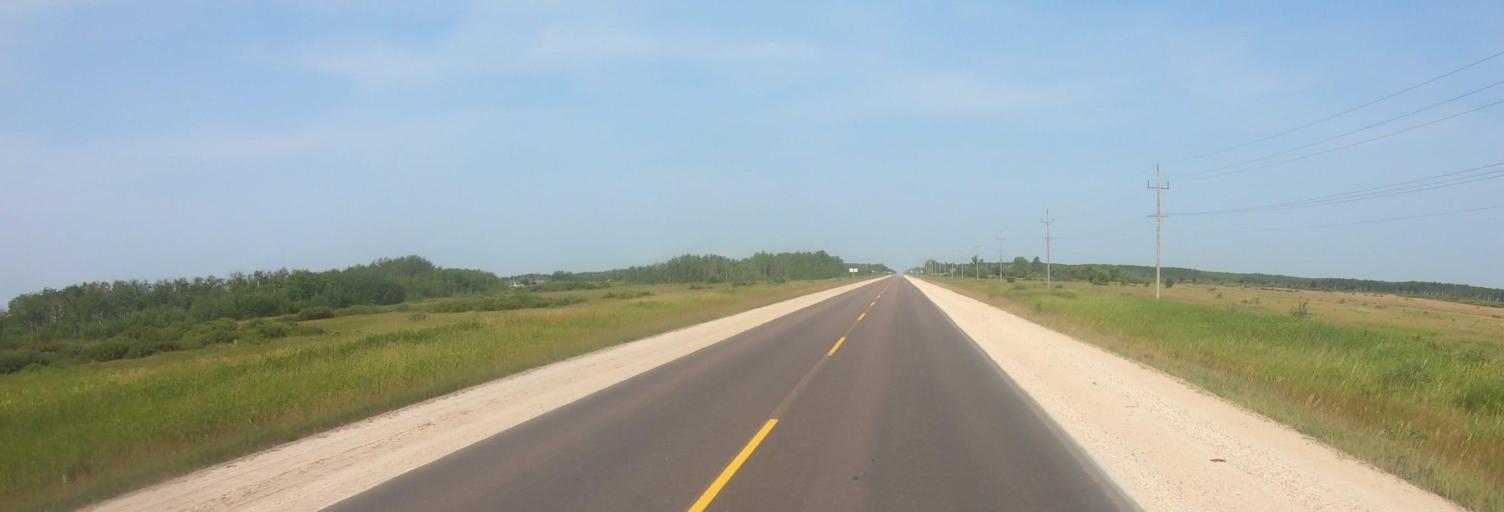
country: CA
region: Manitoba
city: La Broquerie
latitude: 49.2797
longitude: -96.5013
